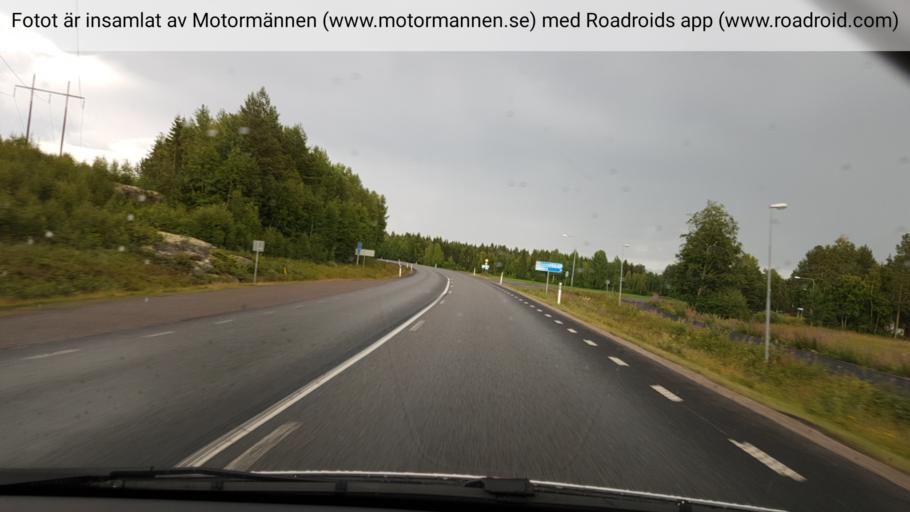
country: SE
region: Vaesterbotten
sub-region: Umea Kommun
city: Roback
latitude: 63.8558
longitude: 20.0965
